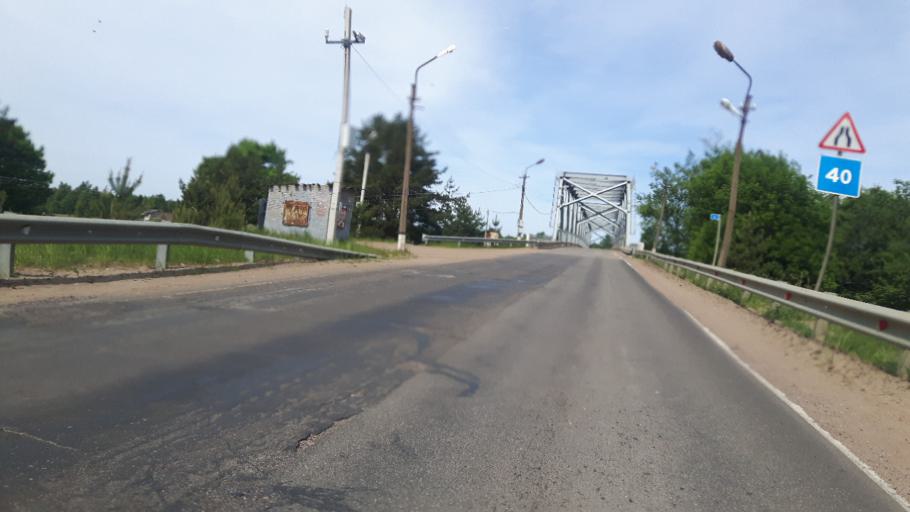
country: RU
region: Leningrad
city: Ust'-Luga
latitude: 59.6515
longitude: 28.2596
